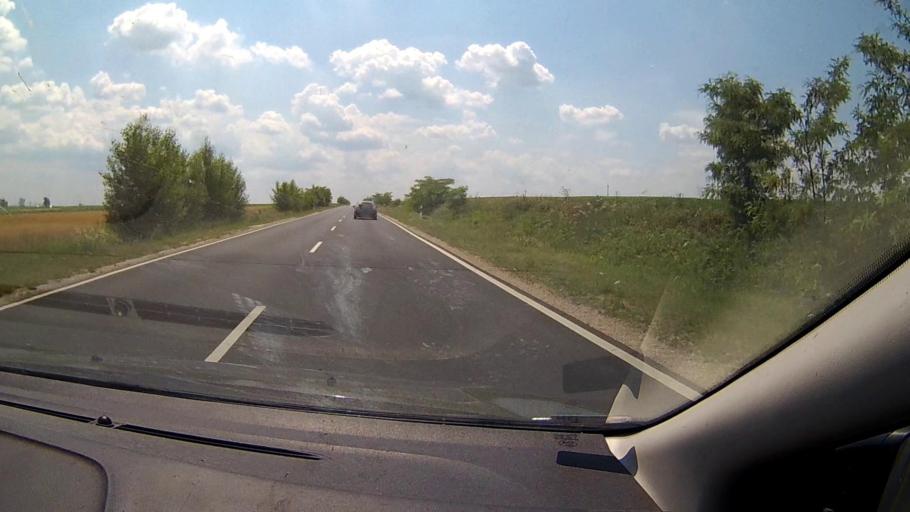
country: HU
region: Komarom-Esztergom
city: Tata
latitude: 47.6001
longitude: 18.3185
